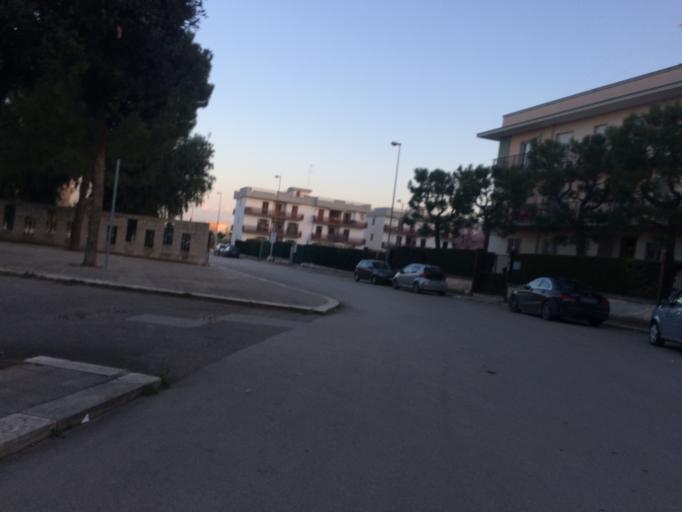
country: IT
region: Apulia
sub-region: Provincia di Bari
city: Ruvo di Puglia
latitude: 41.1149
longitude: 16.4901
